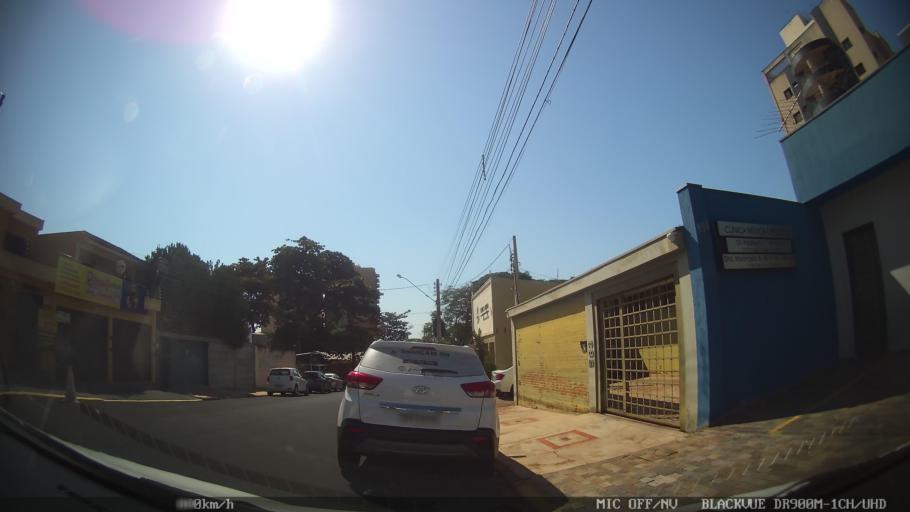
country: BR
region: Sao Paulo
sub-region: Ribeirao Preto
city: Ribeirao Preto
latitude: -21.1901
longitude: -47.8027
